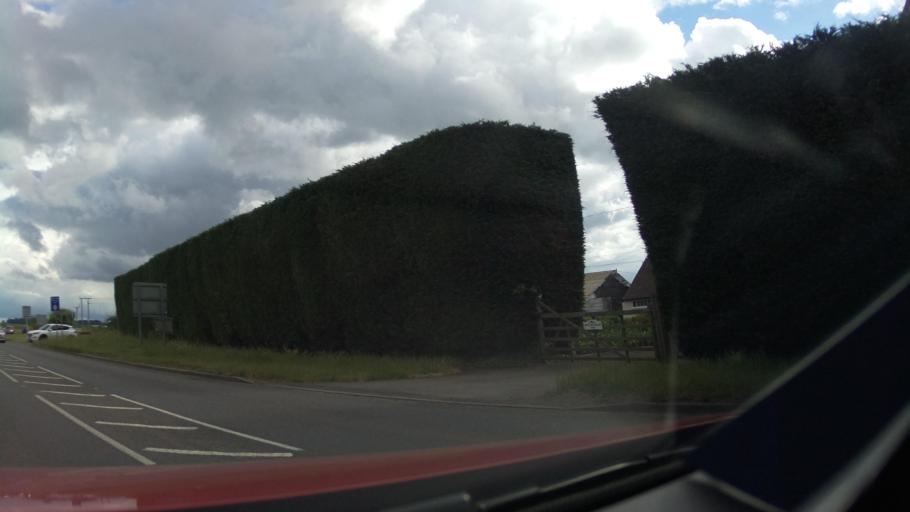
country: GB
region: England
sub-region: Worcestershire
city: Kidderminster
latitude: 52.4412
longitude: -2.2118
